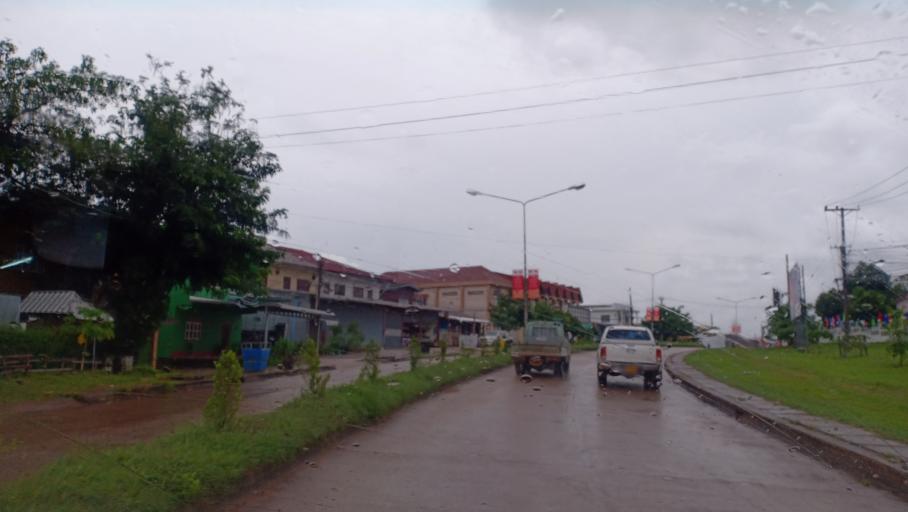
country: LA
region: Khammouan
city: Thakhek
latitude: 17.4024
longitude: 104.8244
